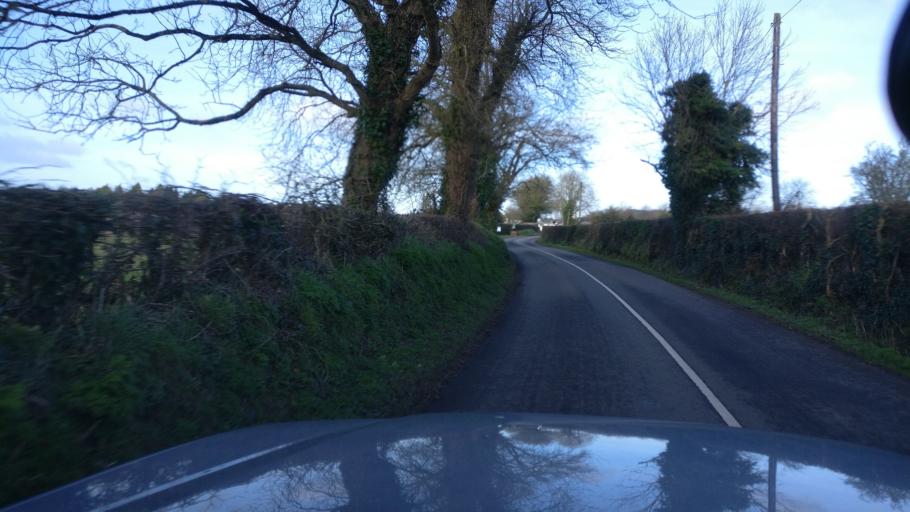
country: IE
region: Leinster
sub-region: Kilkenny
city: Castlecomer
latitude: 52.8865
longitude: -7.1612
